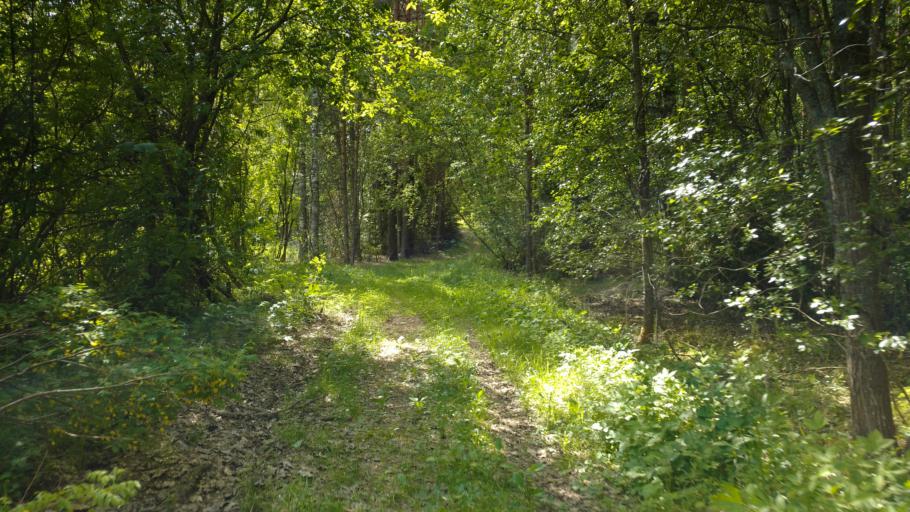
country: FI
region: Varsinais-Suomi
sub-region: Salo
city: Salo
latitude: 60.3709
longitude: 23.1845
